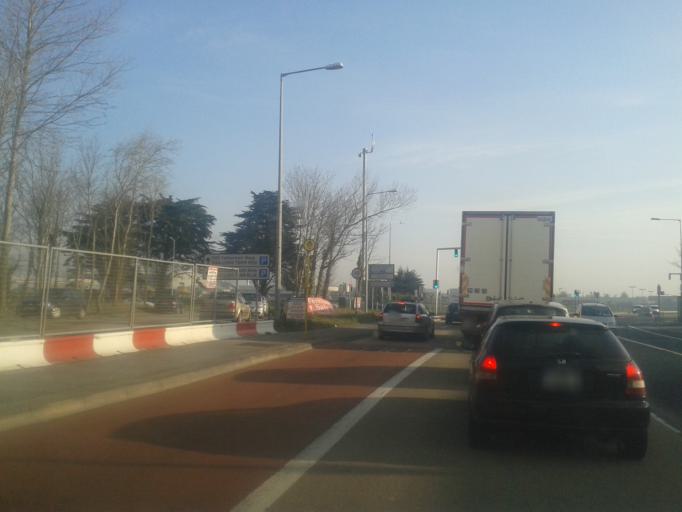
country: IE
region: Leinster
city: Beaumont
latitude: 53.4168
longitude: -6.2390
